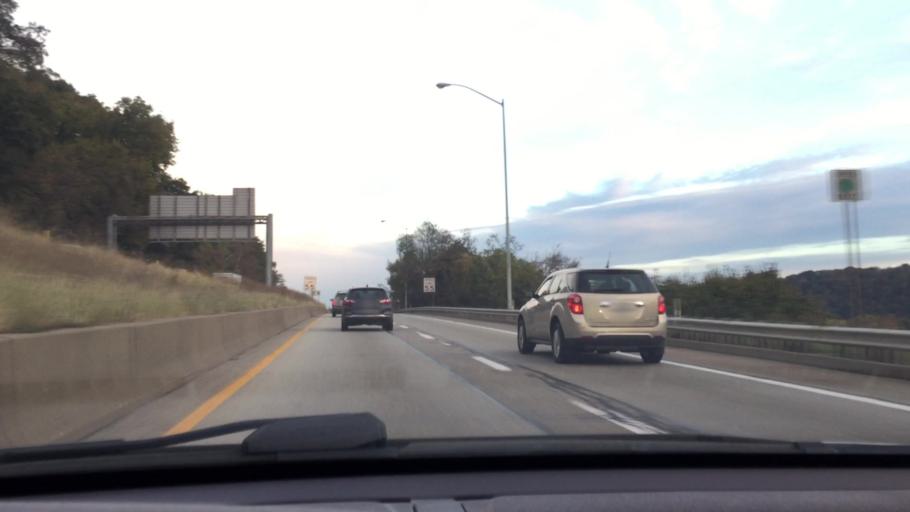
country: US
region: Pennsylvania
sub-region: Allegheny County
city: Aspinwall
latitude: 40.4946
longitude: -79.9055
